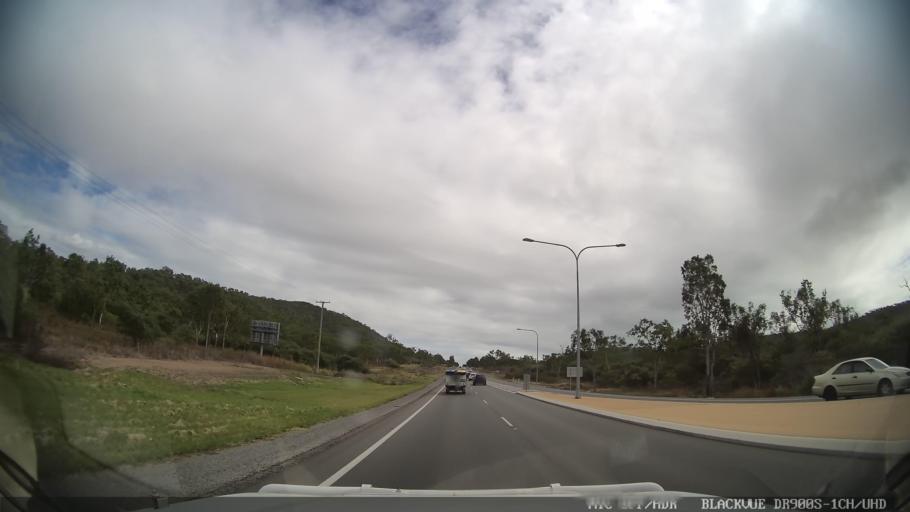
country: AU
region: Queensland
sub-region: Townsville
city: Townsville
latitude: -19.3700
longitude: 146.8961
